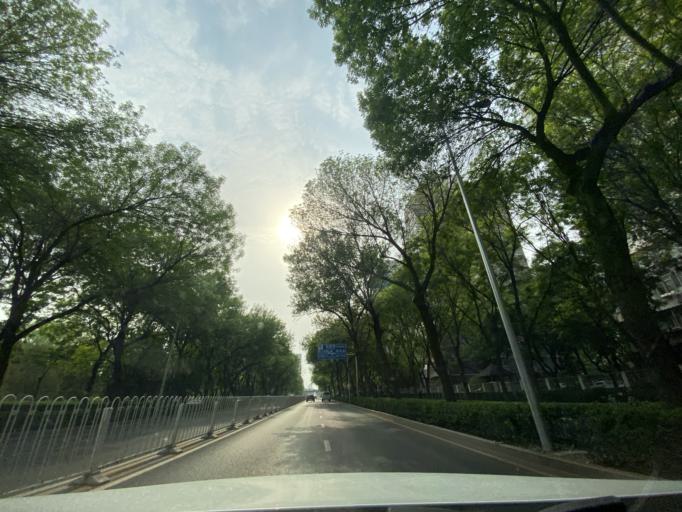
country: CN
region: Beijing
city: Qinghe
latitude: 39.9753
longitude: 116.3521
